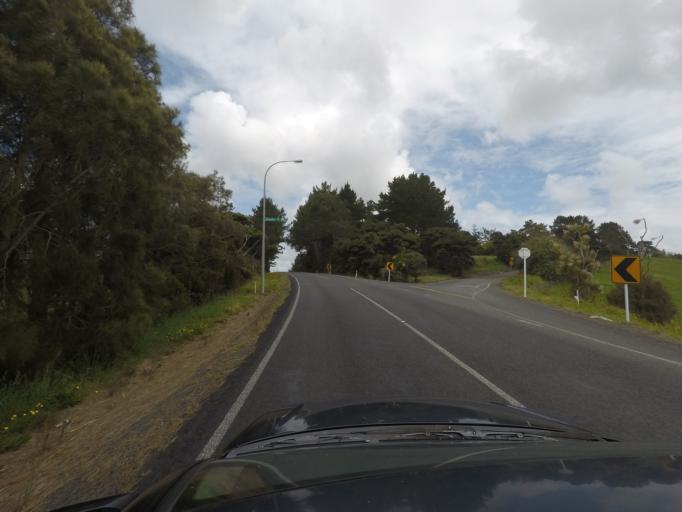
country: NZ
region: Auckland
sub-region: Auckland
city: Parakai
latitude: -36.6376
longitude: 174.5062
